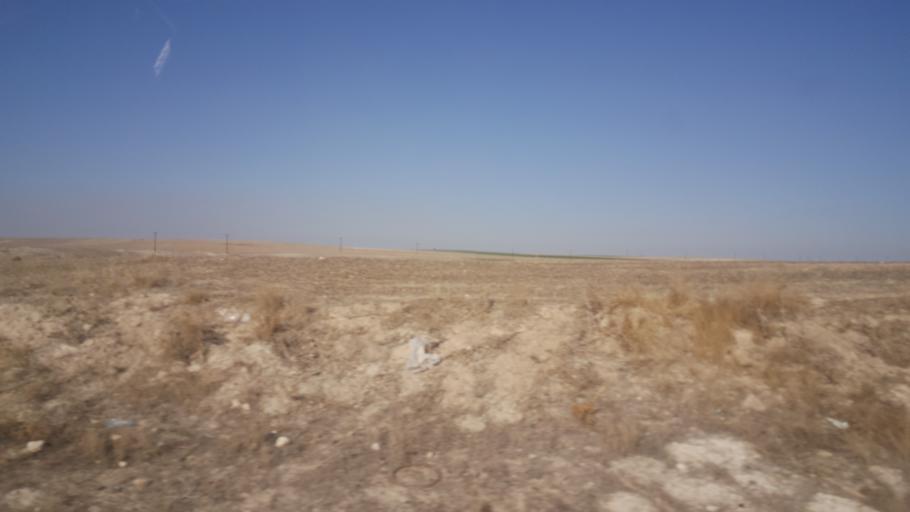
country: TR
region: Konya
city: Celtik
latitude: 39.0613
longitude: 31.8642
